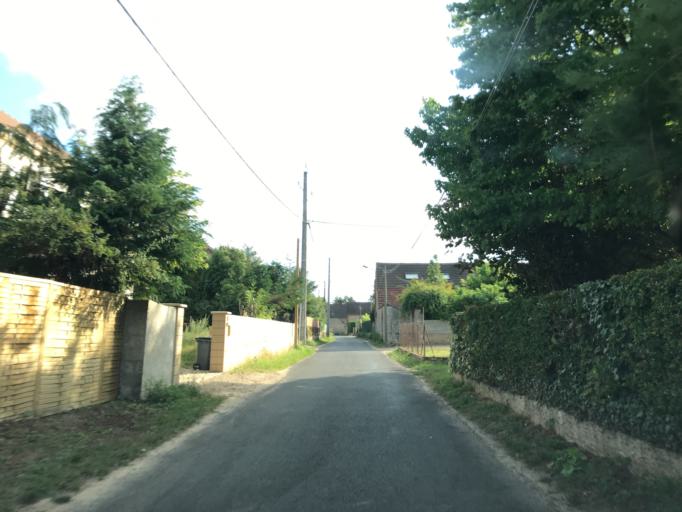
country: FR
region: Haute-Normandie
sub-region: Departement de l'Eure
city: Courcelles-sur-Seine
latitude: 49.1643
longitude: 1.4172
